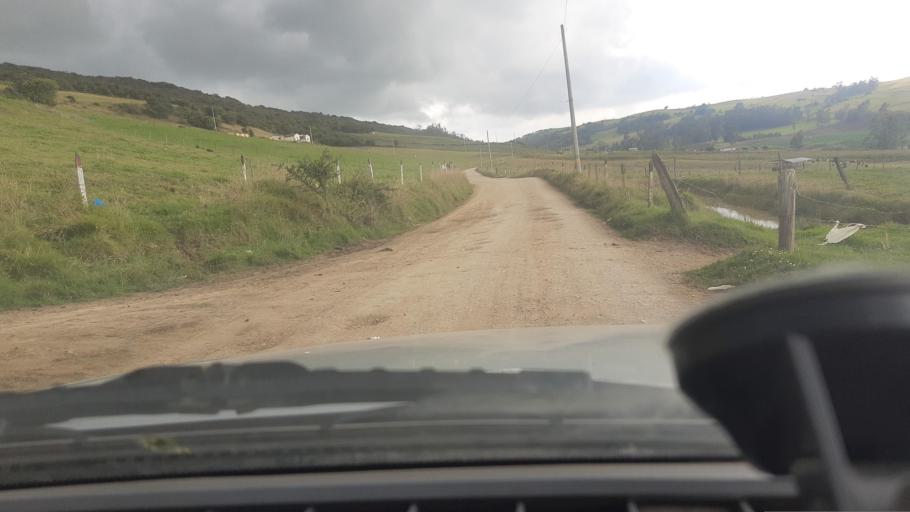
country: CO
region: Cundinamarca
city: Suesca
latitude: 5.1679
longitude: -73.7714
